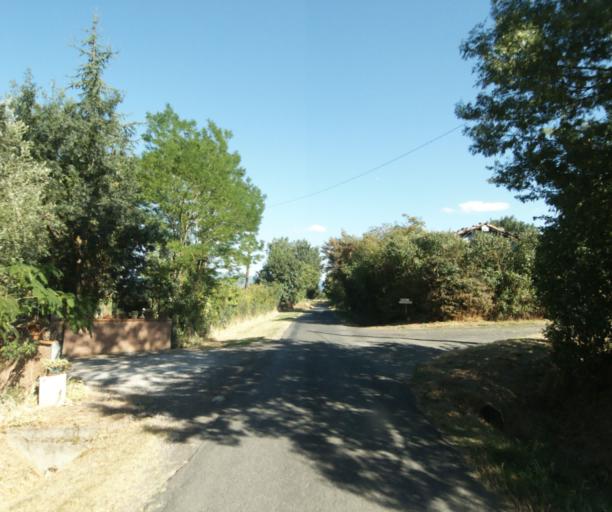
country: FR
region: Midi-Pyrenees
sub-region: Departement de la Haute-Garonne
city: Saint-Felix-Lauragais
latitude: 43.5050
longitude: 1.9412
